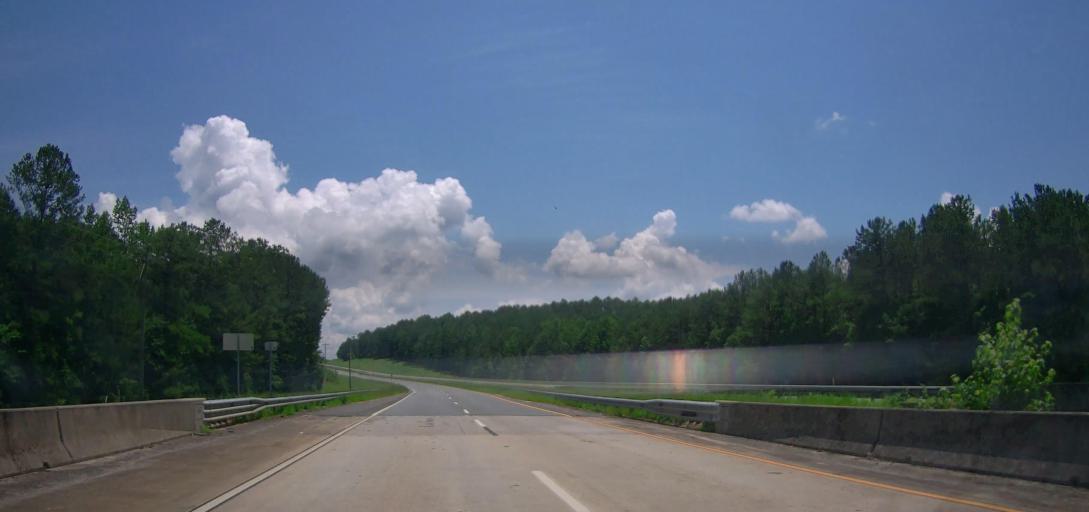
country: US
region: Georgia
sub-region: Upson County
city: Thomaston
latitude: 32.7948
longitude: -84.2653
